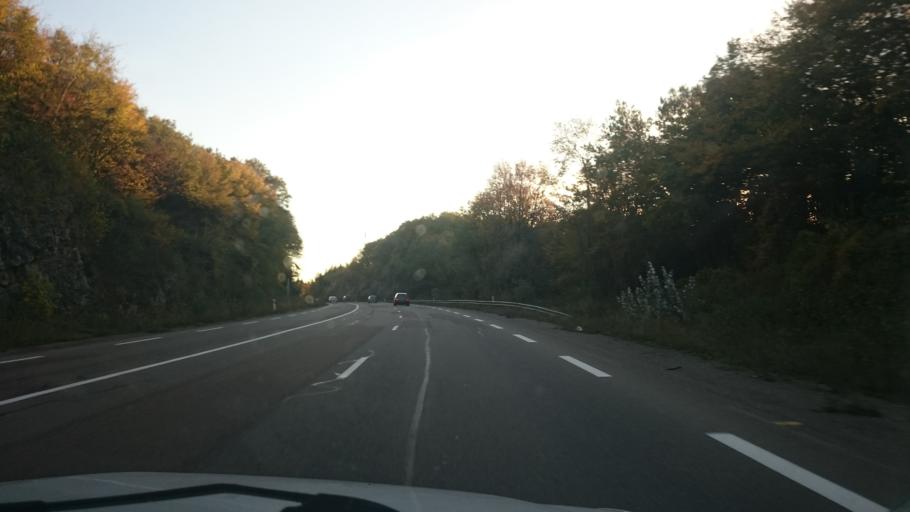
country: FR
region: Franche-Comte
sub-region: Departement du Jura
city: Mouchard
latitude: 46.9745
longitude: 5.8045
